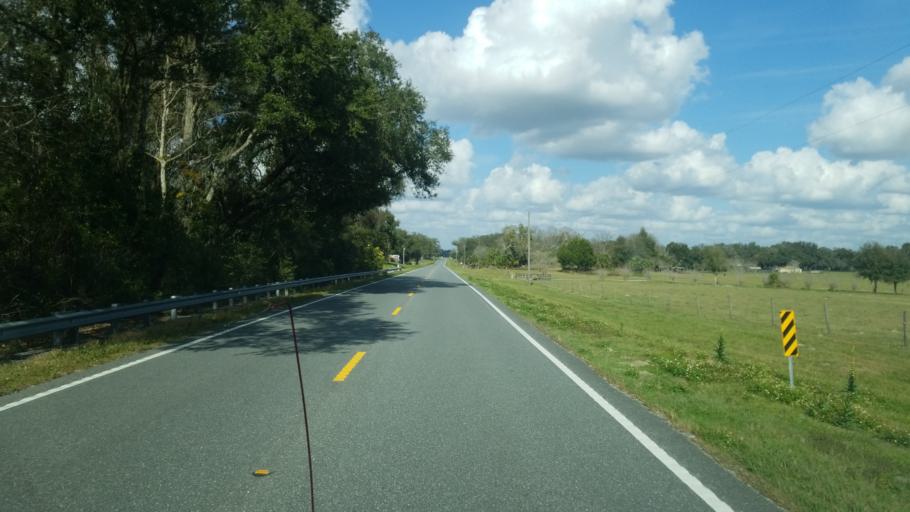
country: US
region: Florida
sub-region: Sumter County
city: Wildwood
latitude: 28.9123
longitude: -82.1200
